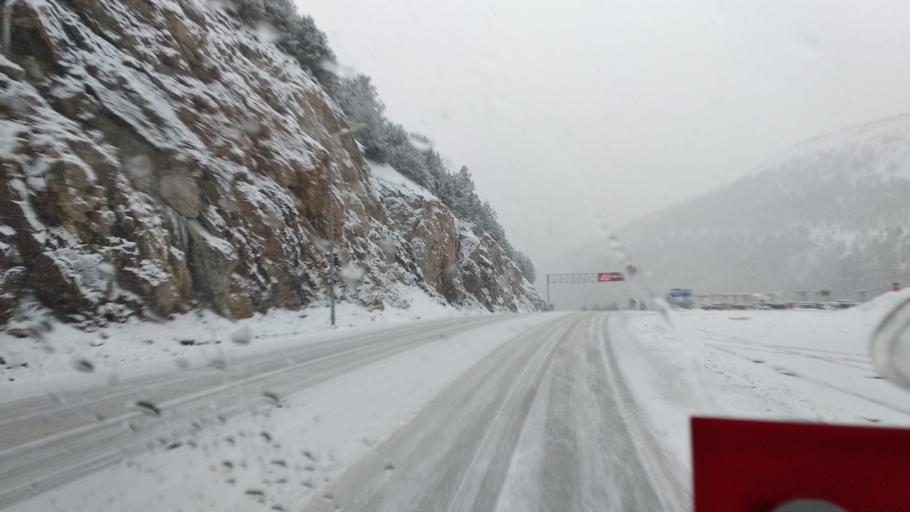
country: TR
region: Gumushane
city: Torul
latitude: 40.6562
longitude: 39.4015
